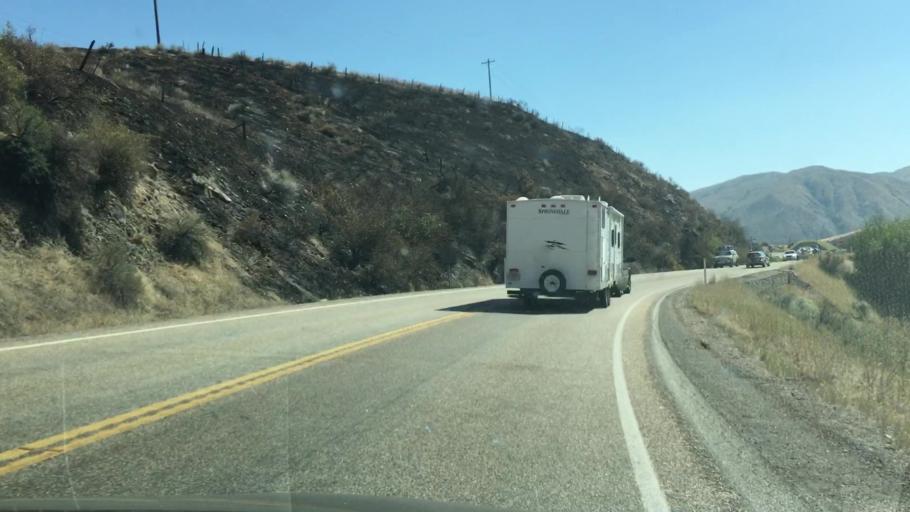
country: US
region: Idaho
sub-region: Gem County
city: Emmett
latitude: 44.0022
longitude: -116.1803
